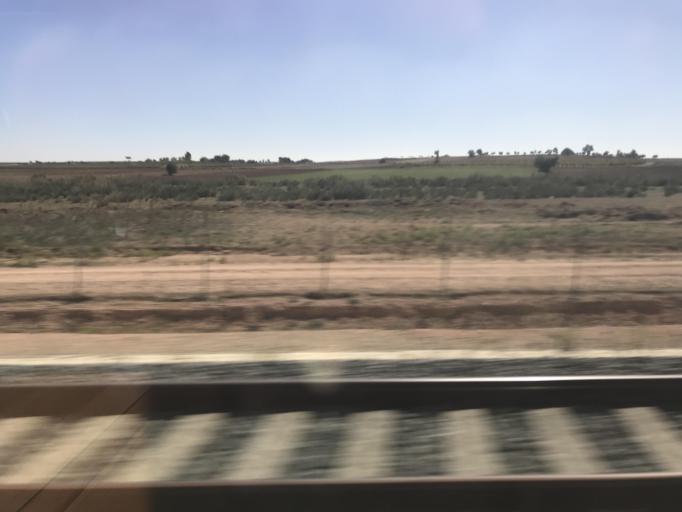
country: ES
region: Castille-La Mancha
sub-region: Provincia de Cuenca
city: Zarza de Tajo
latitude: 39.9795
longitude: -3.1433
